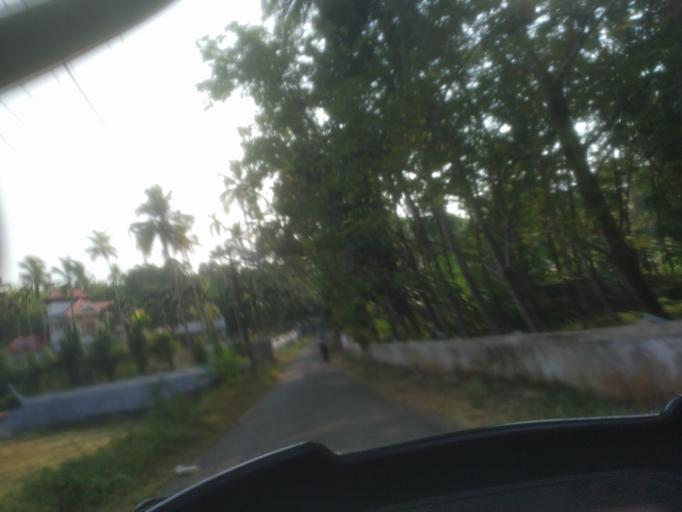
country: IN
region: Kerala
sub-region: Ernakulam
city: Piravam
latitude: 9.8493
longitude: 76.5296
